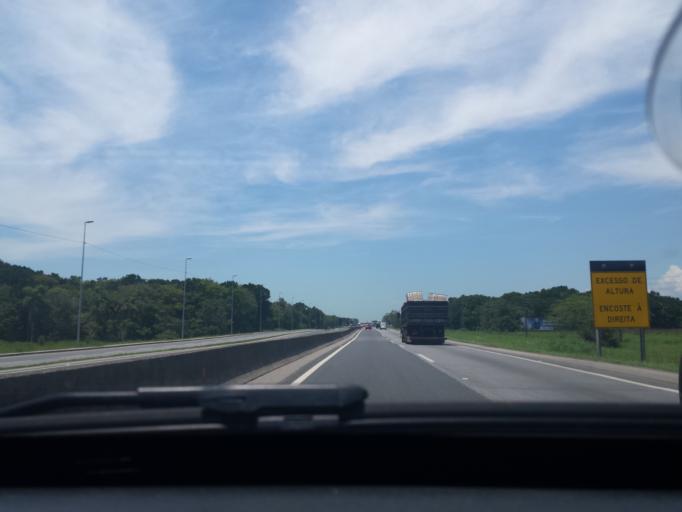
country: BR
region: Santa Catarina
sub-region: Porto Belo
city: Porto Belo
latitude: -27.1501
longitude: -48.6107
